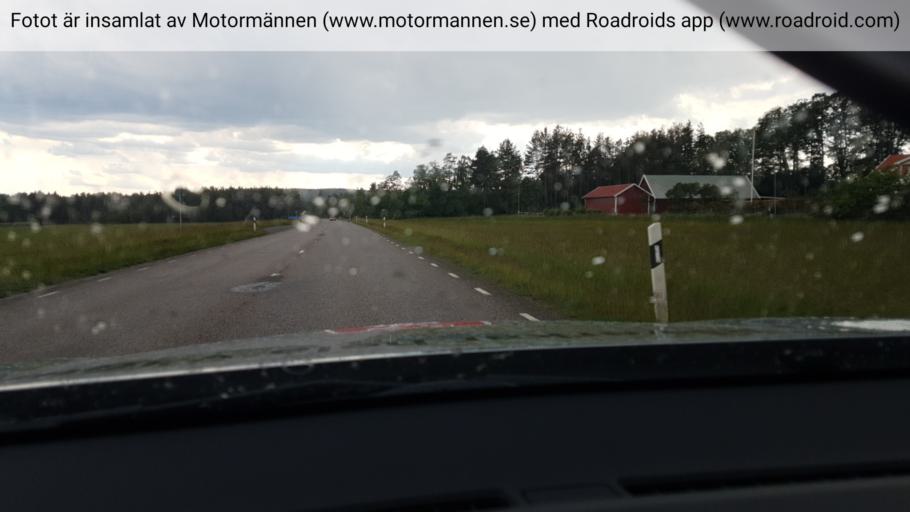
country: SE
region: Vaestra Goetaland
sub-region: Hjo Kommun
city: Hjo
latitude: 58.3158
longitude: 14.2599
